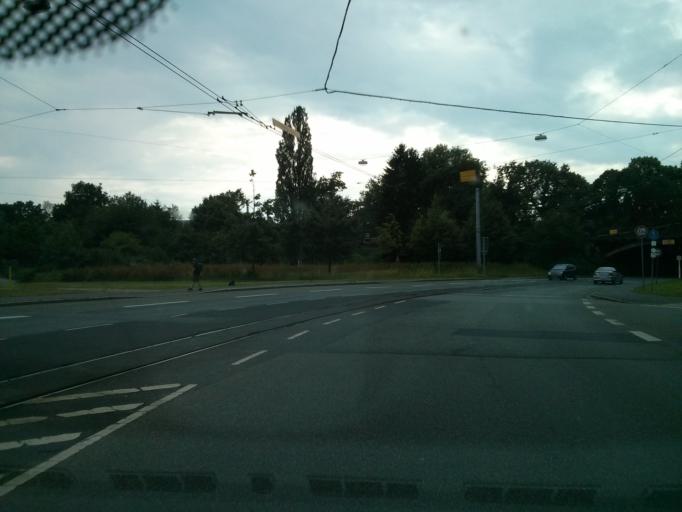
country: DE
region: North Rhine-Westphalia
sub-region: Regierungsbezirk Dusseldorf
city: Krefeld
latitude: 51.3349
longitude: 6.6295
